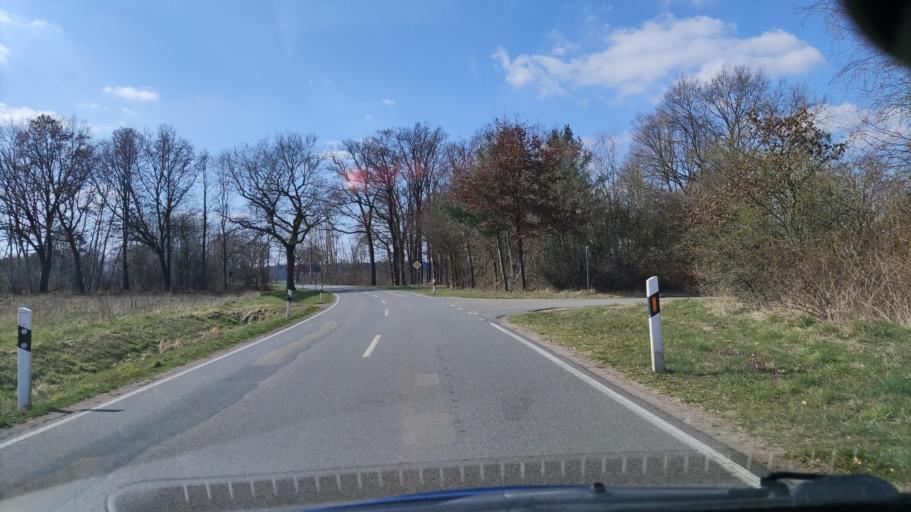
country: DE
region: Lower Saxony
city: Trebel
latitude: 53.0337
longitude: 11.2927
